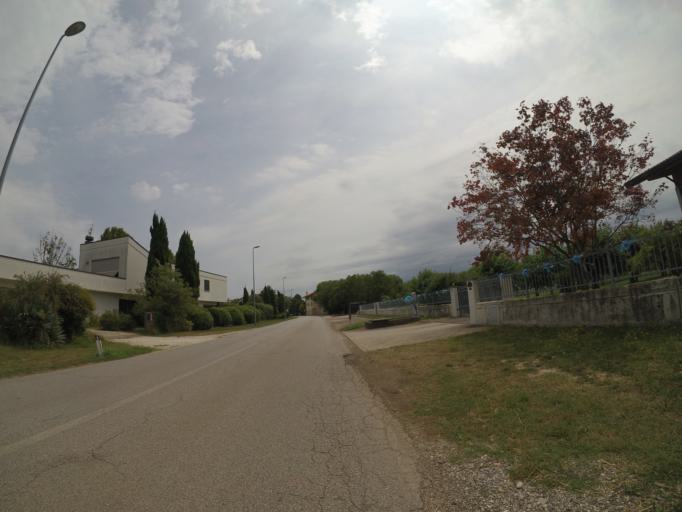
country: IT
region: Friuli Venezia Giulia
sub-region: Provincia di Udine
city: Sedegliano
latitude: 46.0025
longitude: 12.9938
